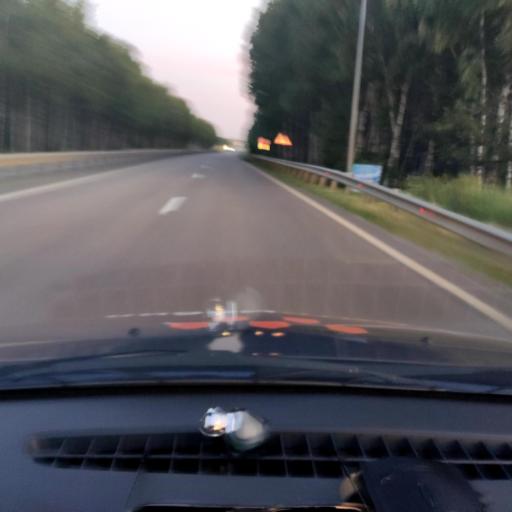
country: RU
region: Belgorod
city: Staryy Oskol
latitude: 51.4119
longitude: 37.8843
